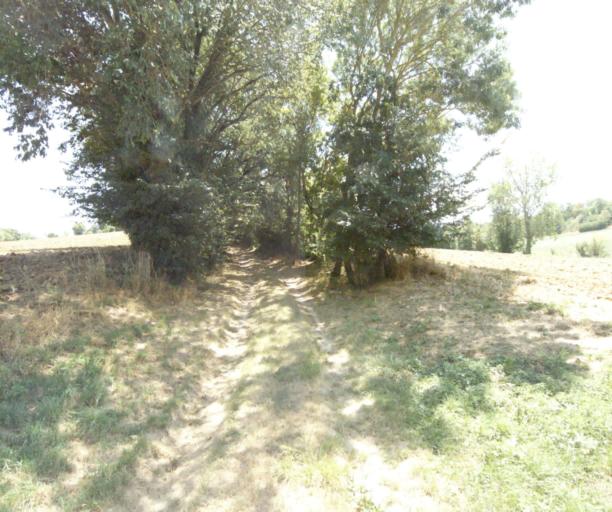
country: FR
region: Midi-Pyrenees
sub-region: Departement de la Haute-Garonne
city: Saint-Felix-Lauragais
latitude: 43.4844
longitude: 1.8560
